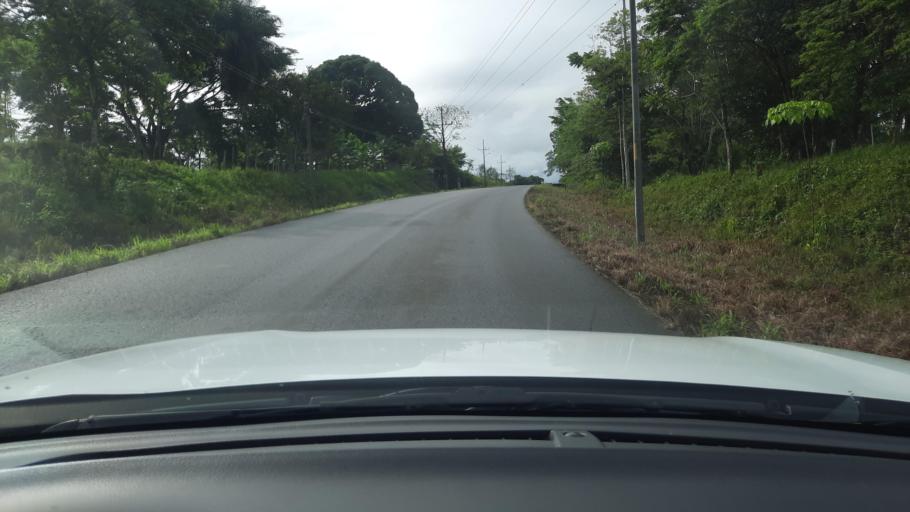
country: CR
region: Alajuela
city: San Jose
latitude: 10.9441
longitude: -85.1165
